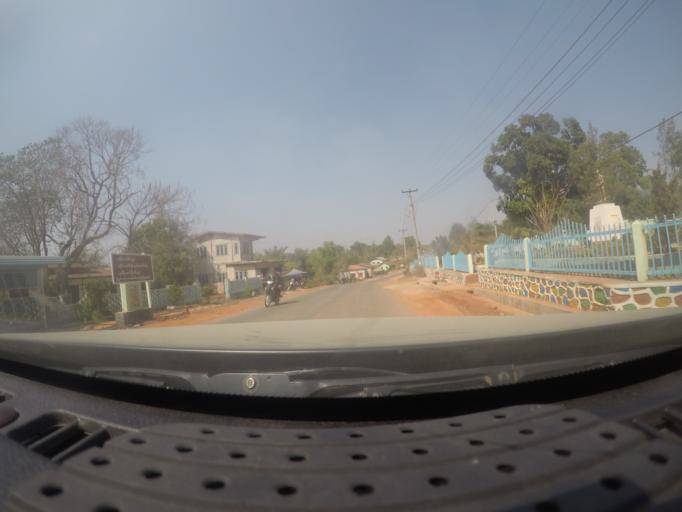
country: MM
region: Mandalay
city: Kyaukse
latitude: 21.1632
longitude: 96.4438
